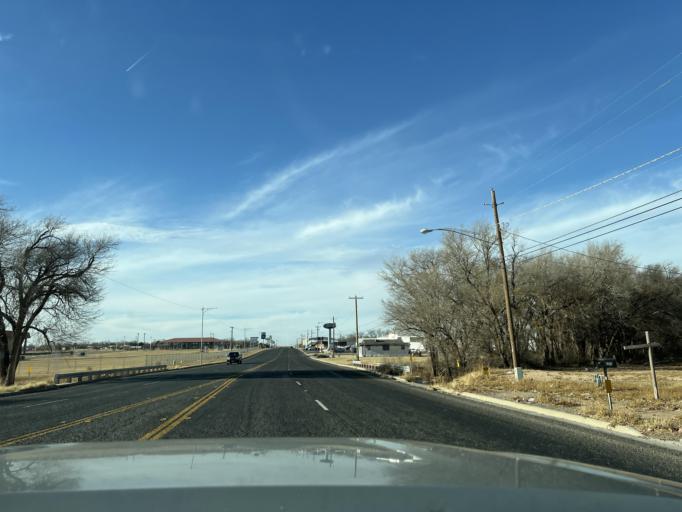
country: US
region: Texas
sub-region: Scurry County
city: Snyder
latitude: 32.7055
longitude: -100.8842
